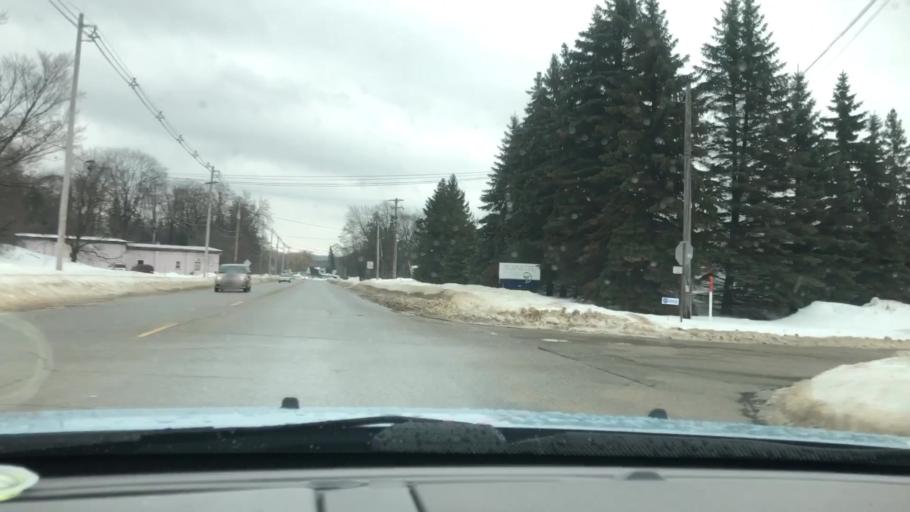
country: US
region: Michigan
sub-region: Charlevoix County
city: East Jordan
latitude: 45.1536
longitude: -85.1230
